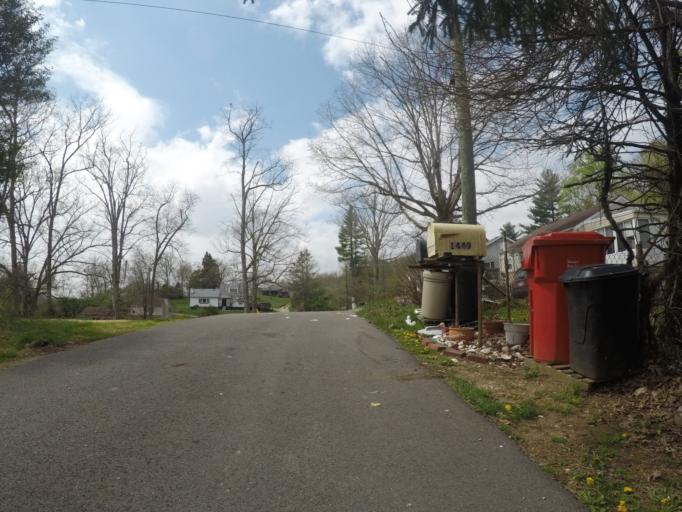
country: US
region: Ohio
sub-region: Lawrence County
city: Burlington
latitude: 38.3867
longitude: -82.5135
